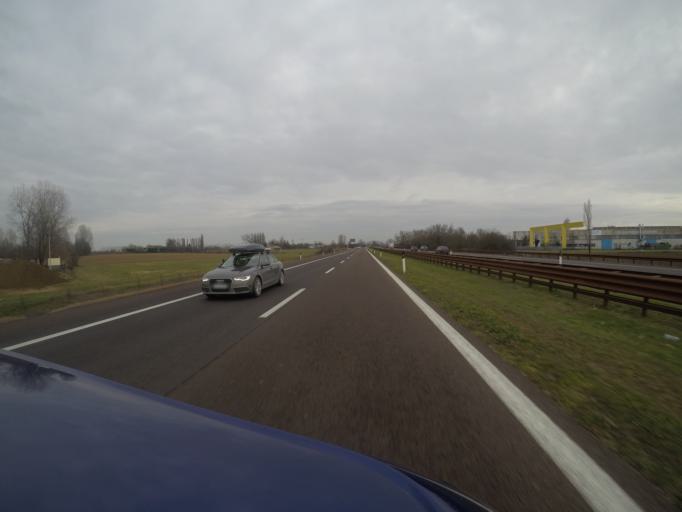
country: IT
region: Emilia-Romagna
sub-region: Provincia di Modena
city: Campogalliano
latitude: 44.6985
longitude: 10.8495
